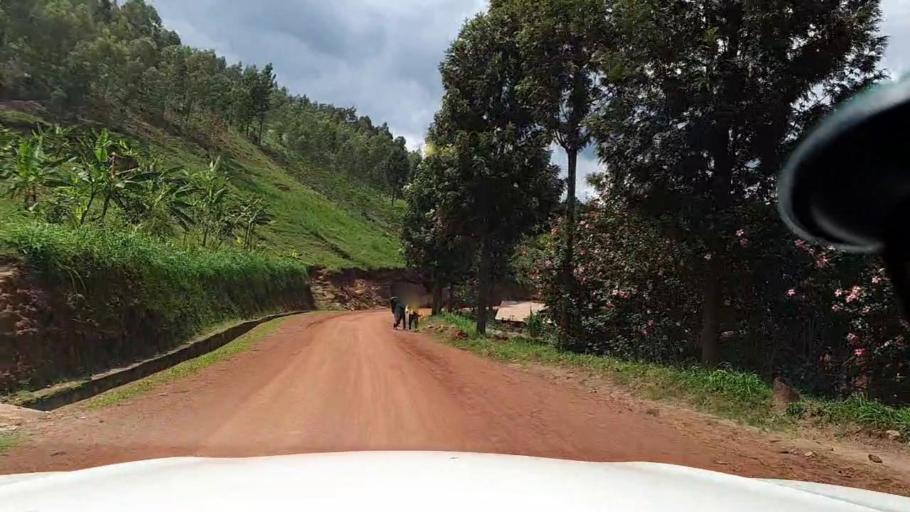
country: RW
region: Northern Province
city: Byumba
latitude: -1.7525
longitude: 29.8458
